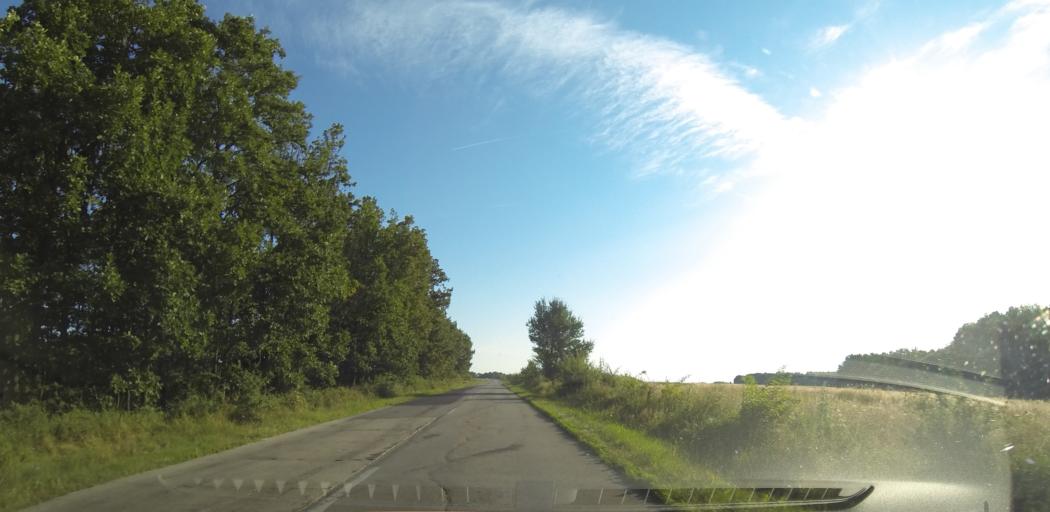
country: RO
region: Valcea
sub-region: Comuna Balcesti
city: Balcesti
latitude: 44.5988
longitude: 23.9274
